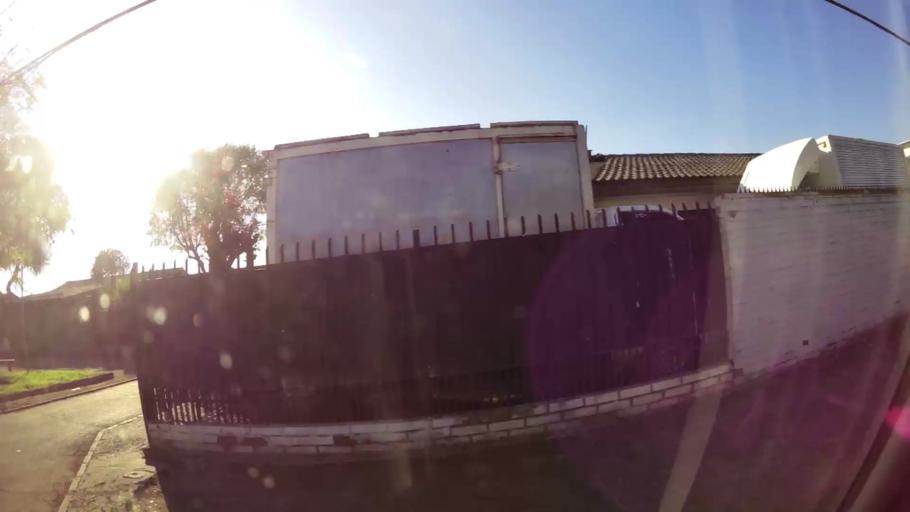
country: CL
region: Santiago Metropolitan
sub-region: Provincia de Santiago
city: Lo Prado
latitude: -33.4847
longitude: -70.7585
